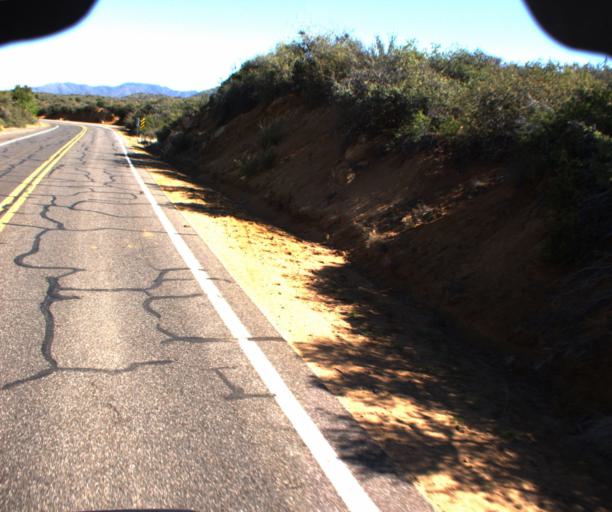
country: US
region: Arizona
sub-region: Yavapai County
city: Prescott
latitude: 34.4252
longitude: -112.5795
